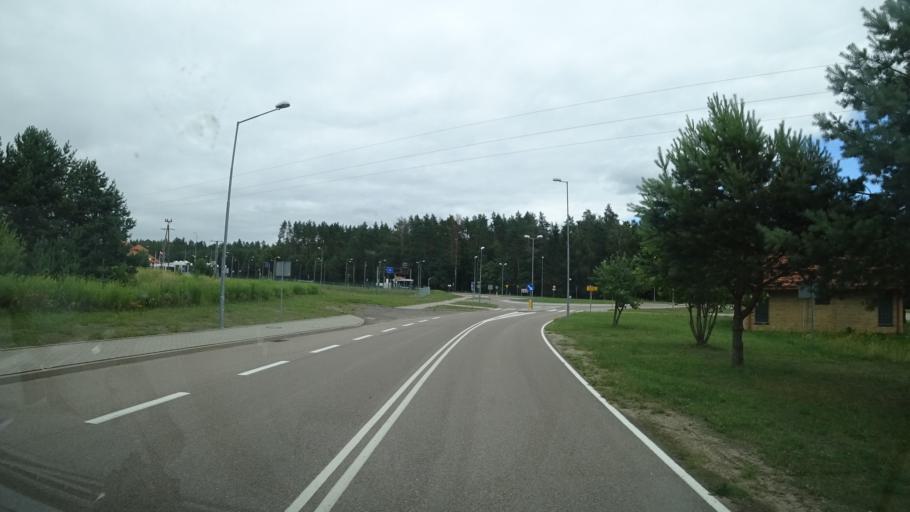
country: PL
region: Warmian-Masurian Voivodeship
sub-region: Powiat goldapski
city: Goldap
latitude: 54.3374
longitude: 22.2949
